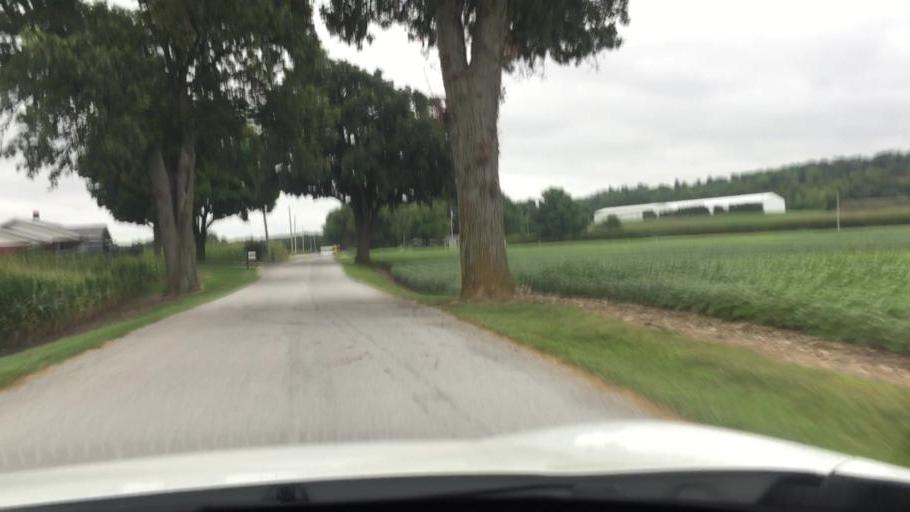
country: US
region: Ohio
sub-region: Clark County
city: Northridge
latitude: 39.9925
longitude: -83.6632
